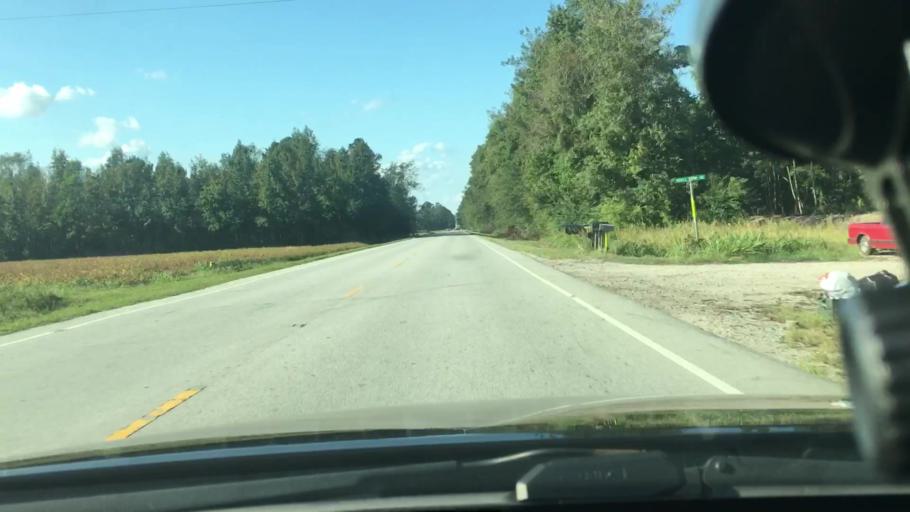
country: US
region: North Carolina
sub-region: Craven County
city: New Bern
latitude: 35.1716
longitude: -77.0434
